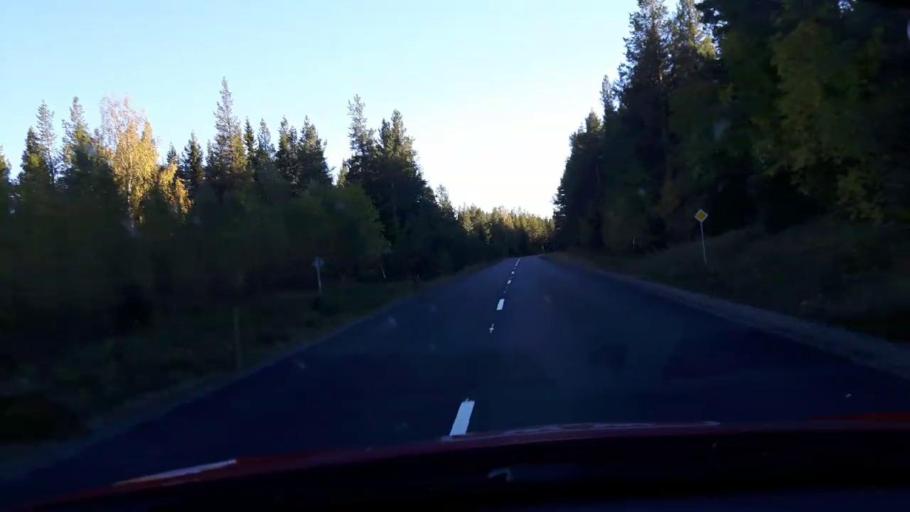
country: SE
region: Jaemtland
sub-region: OEstersunds Kommun
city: Lit
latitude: 63.4722
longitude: 14.8779
